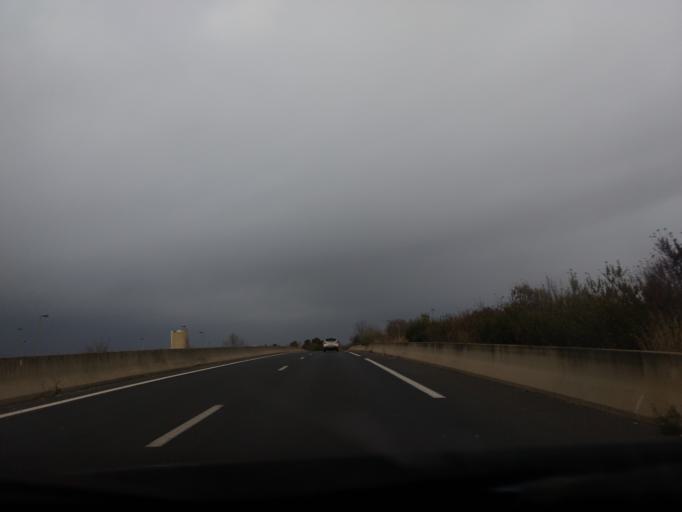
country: FR
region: Languedoc-Roussillon
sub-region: Departement de l'Herault
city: Lattes
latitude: 43.5539
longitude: 3.8932
